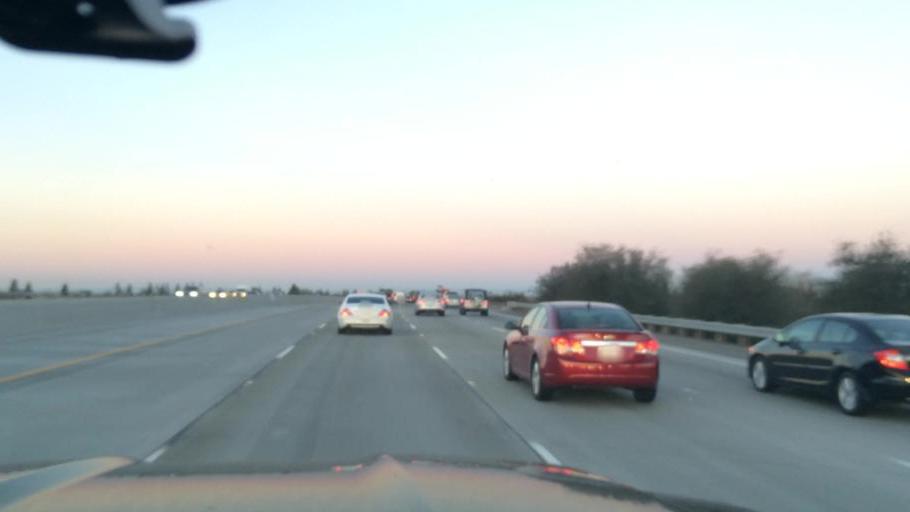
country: US
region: California
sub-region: Sacramento County
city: Rio Linda
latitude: 38.6416
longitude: -121.4464
